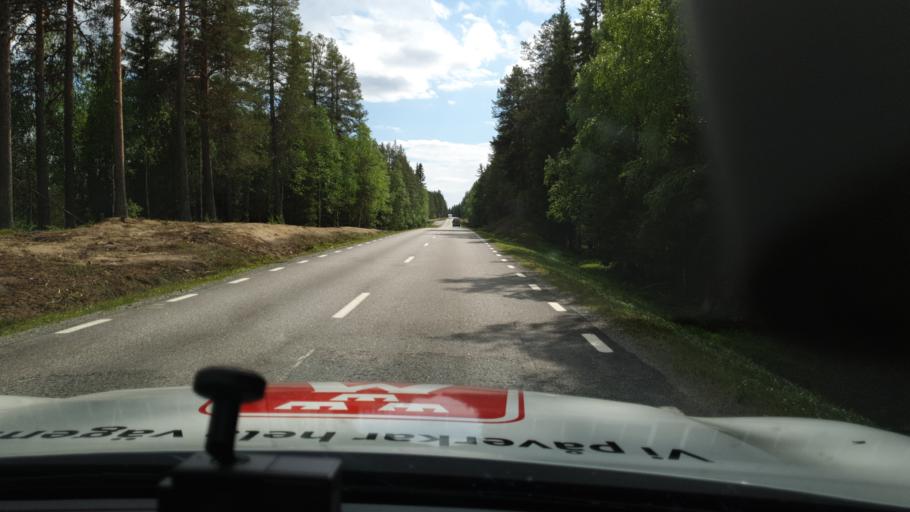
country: SE
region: Vaesterbotten
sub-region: Sorsele Kommun
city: Sorsele
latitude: 65.2662
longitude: 17.6702
